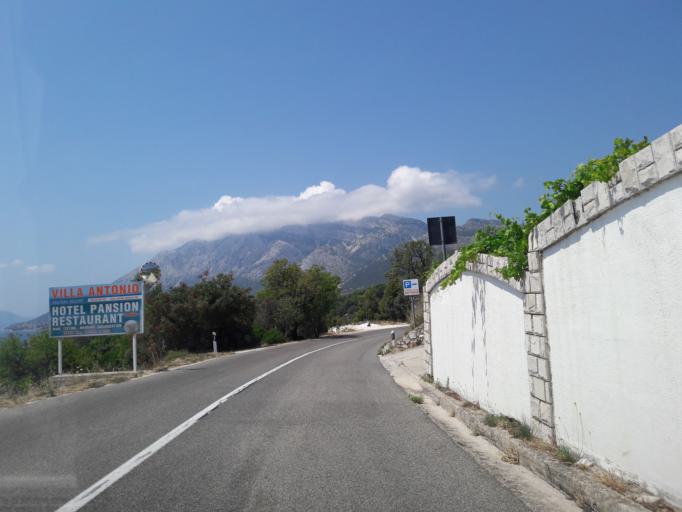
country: HR
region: Dubrovacko-Neretvanska
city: Orebic
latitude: 42.9753
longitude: 17.2315
